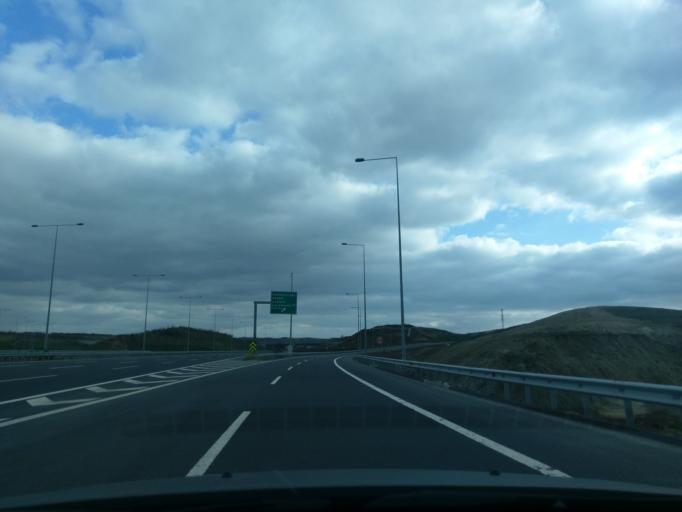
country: TR
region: Istanbul
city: Kemerburgaz
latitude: 41.2364
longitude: 28.8358
